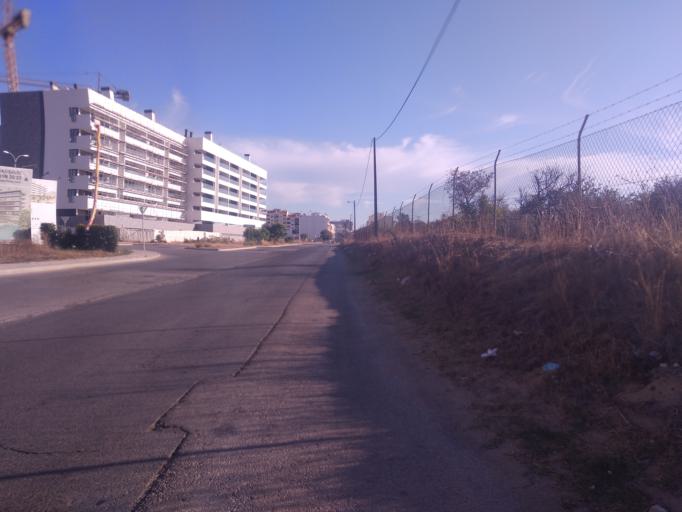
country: PT
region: Faro
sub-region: Faro
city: Faro
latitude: 37.0314
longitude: -7.9399
